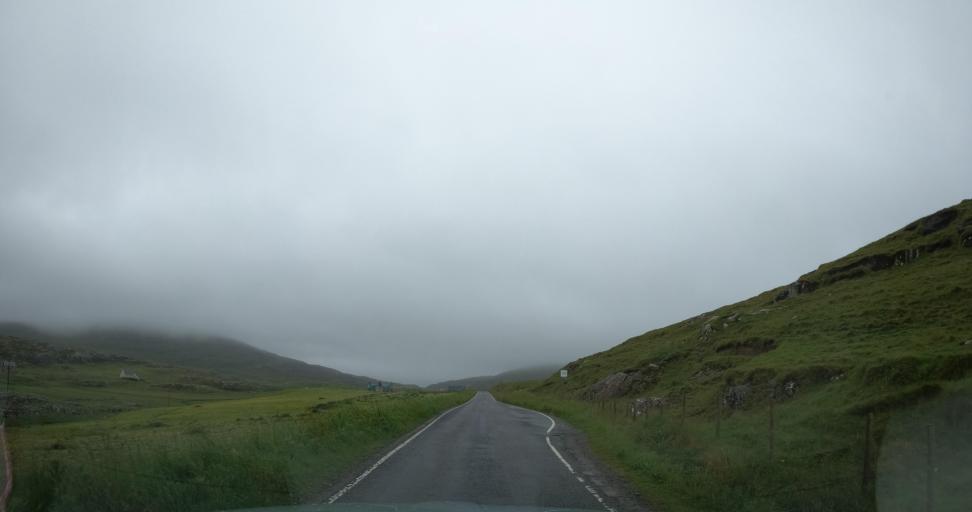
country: GB
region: Scotland
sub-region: Eilean Siar
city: Barra
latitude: 57.0029
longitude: -7.4940
